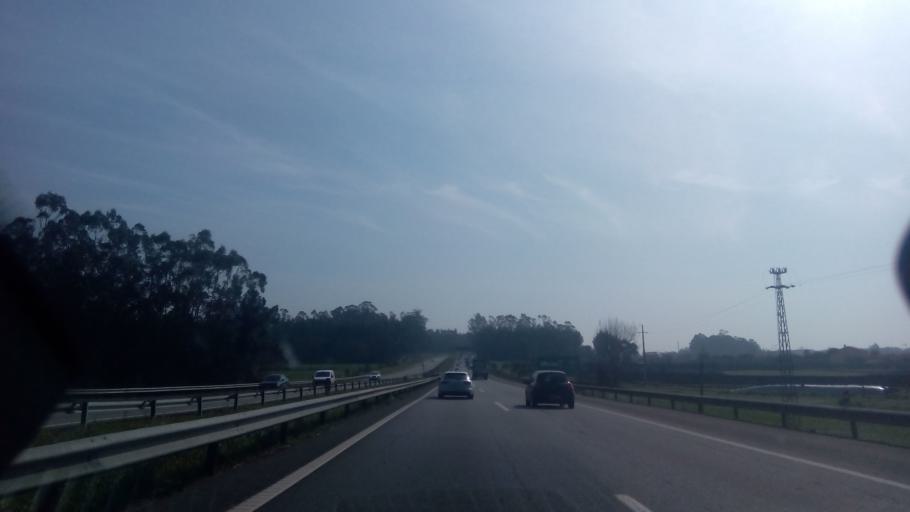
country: PT
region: Porto
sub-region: Vila do Conde
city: Arvore
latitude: 41.3621
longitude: -8.7198
